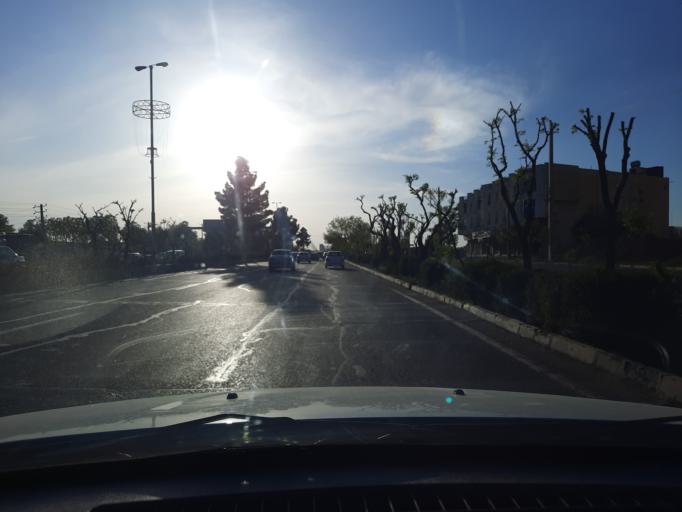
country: IR
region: Qazvin
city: Qazvin
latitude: 36.2621
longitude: 50.0448
